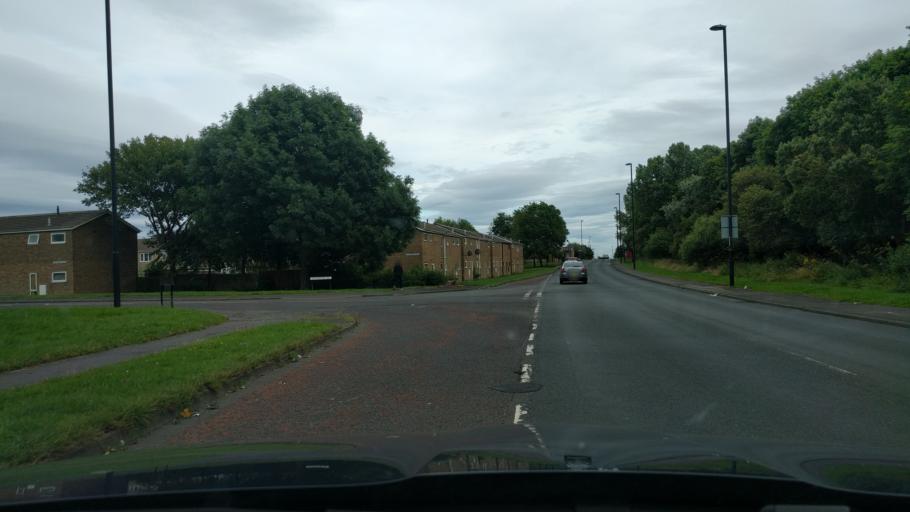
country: GB
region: England
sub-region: Borough of North Tyneside
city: Shiremoor
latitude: 55.0202
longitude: -1.4891
